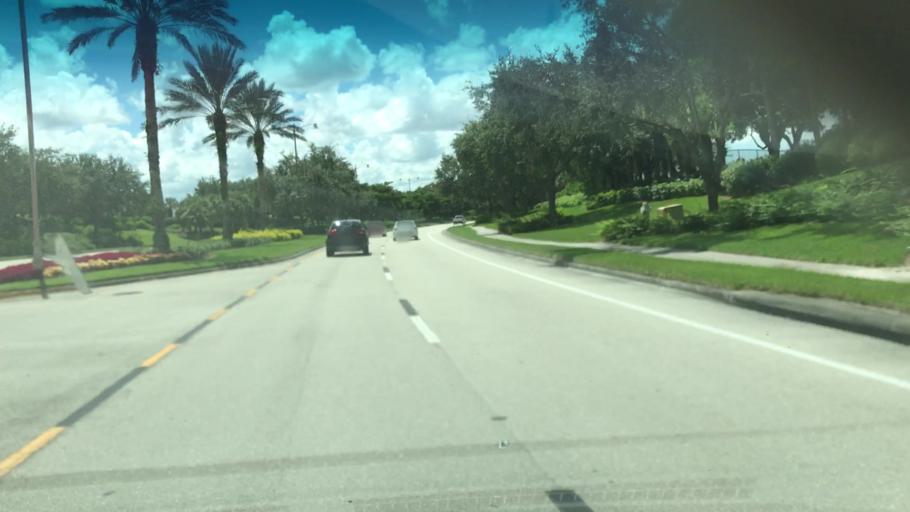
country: US
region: Florida
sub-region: Lee County
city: Estero
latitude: 26.4089
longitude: -81.7824
